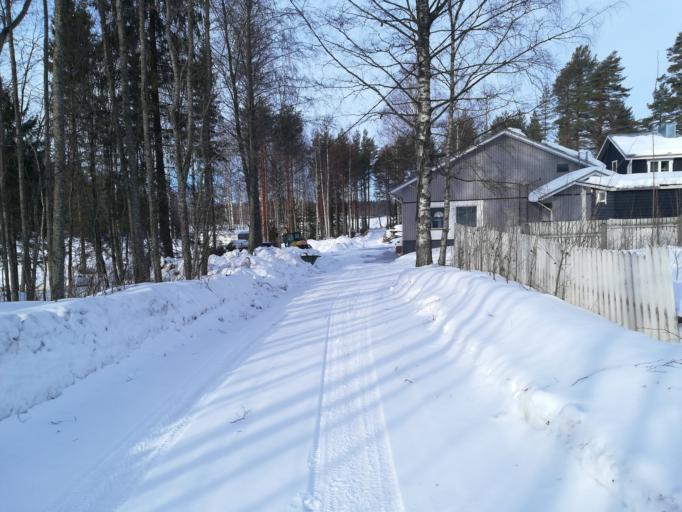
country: FI
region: Southern Savonia
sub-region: Savonlinna
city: Savonlinna
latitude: 61.8289
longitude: 29.0247
